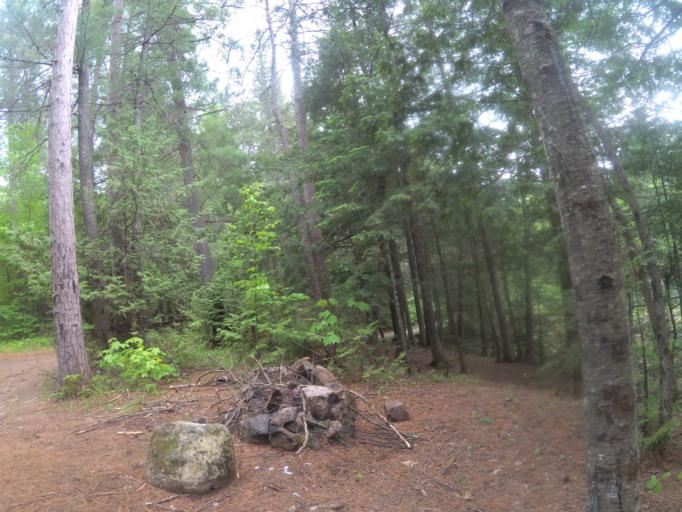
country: CA
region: Ontario
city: Renfrew
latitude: 45.1013
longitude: -76.8346
